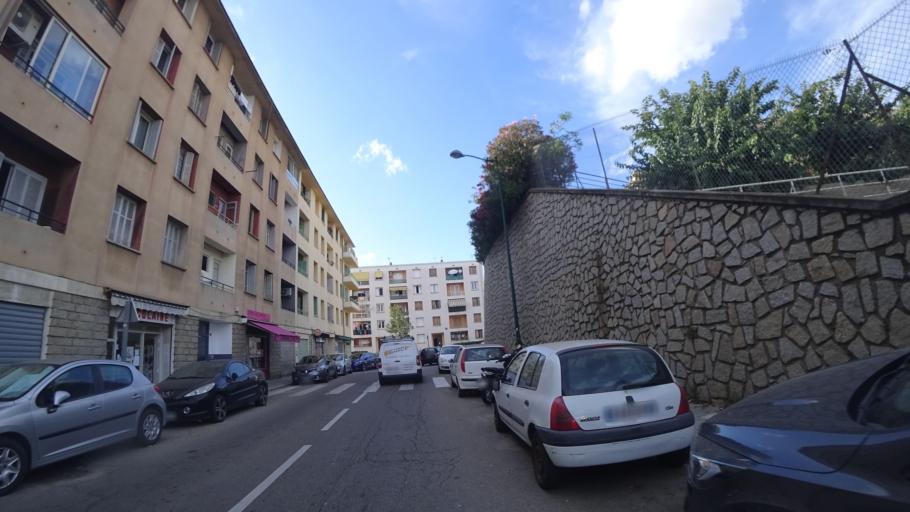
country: FR
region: Corsica
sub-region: Departement de la Corse-du-Sud
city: Ajaccio
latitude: 41.9343
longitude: 8.7437
